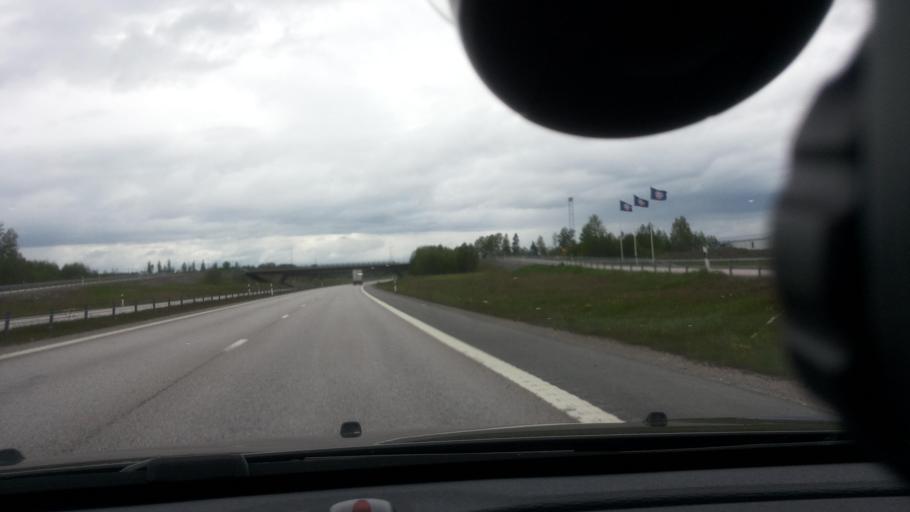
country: SE
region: Uppsala
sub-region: Tierps Kommun
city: Tierp
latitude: 60.3374
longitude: 17.4897
